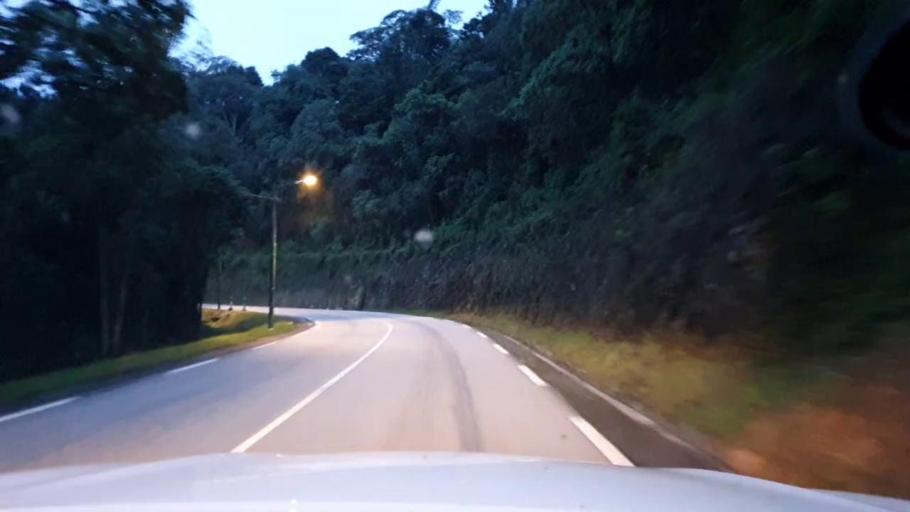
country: RW
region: Southern Province
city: Nzega
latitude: -2.5283
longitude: 29.3778
